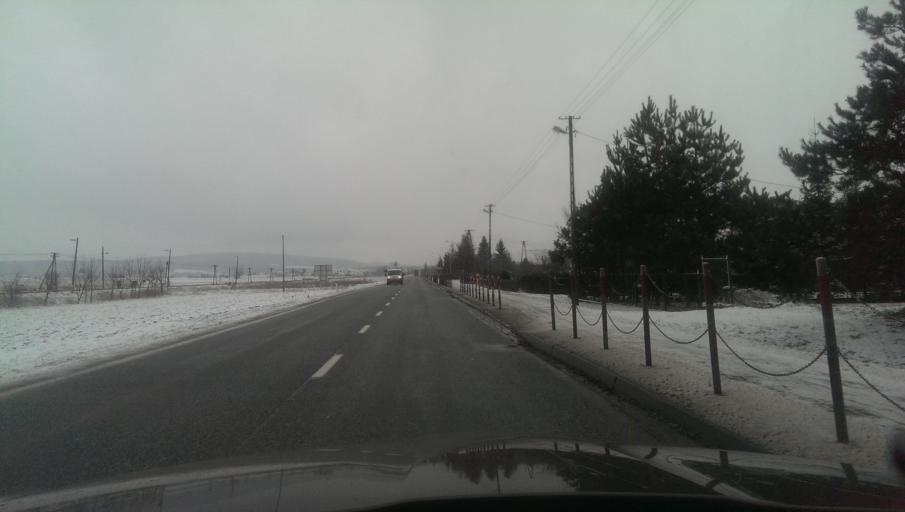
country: PL
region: Subcarpathian Voivodeship
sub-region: Powiat sanocki
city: Zarszyn
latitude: 49.5825
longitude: 22.0246
